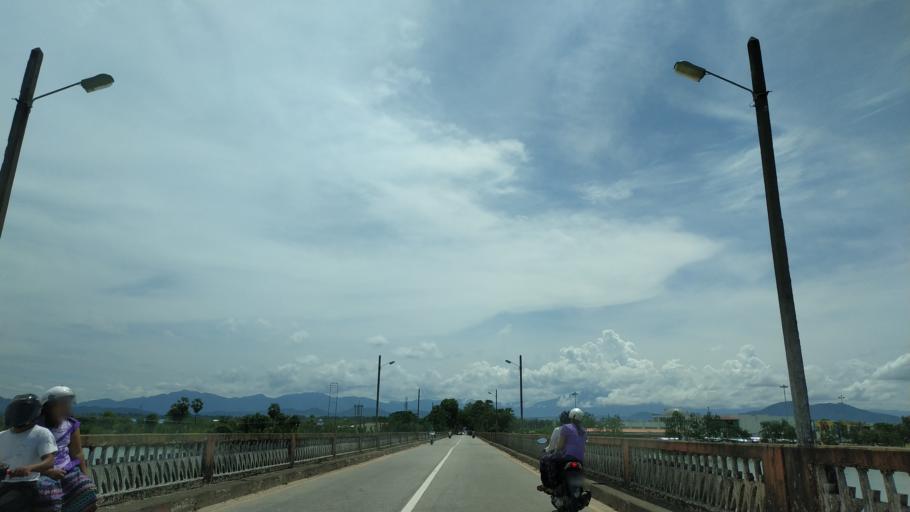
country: MM
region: Tanintharyi
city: Dawei
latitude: 14.0950
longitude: 98.1734
